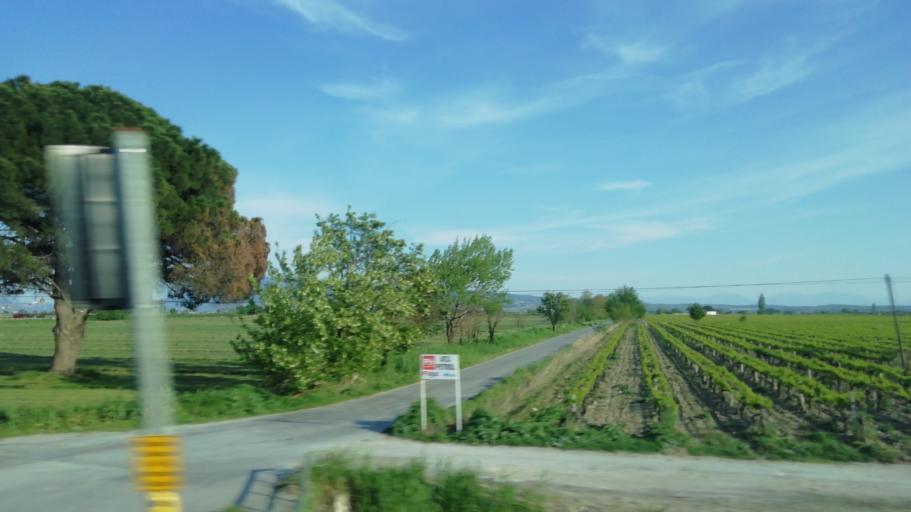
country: TR
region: Manisa
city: Saruhanli
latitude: 38.7453
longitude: 27.6124
